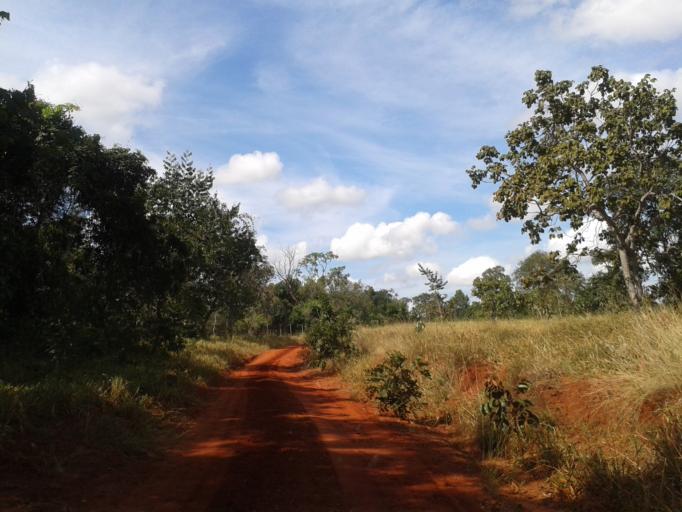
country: BR
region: Minas Gerais
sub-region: Campina Verde
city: Campina Verde
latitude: -19.4457
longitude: -49.6606
